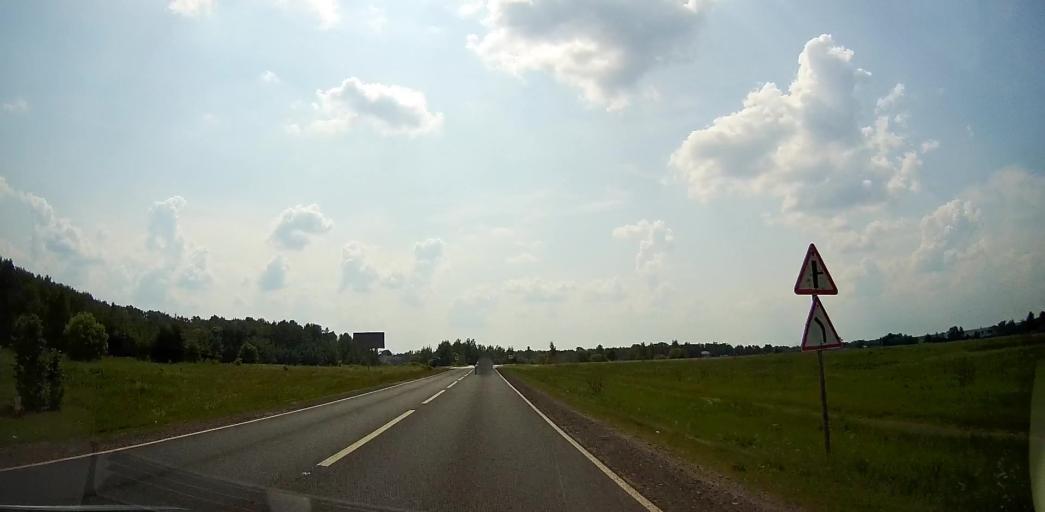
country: RU
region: Moskovskaya
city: Malino
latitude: 55.0979
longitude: 38.1668
